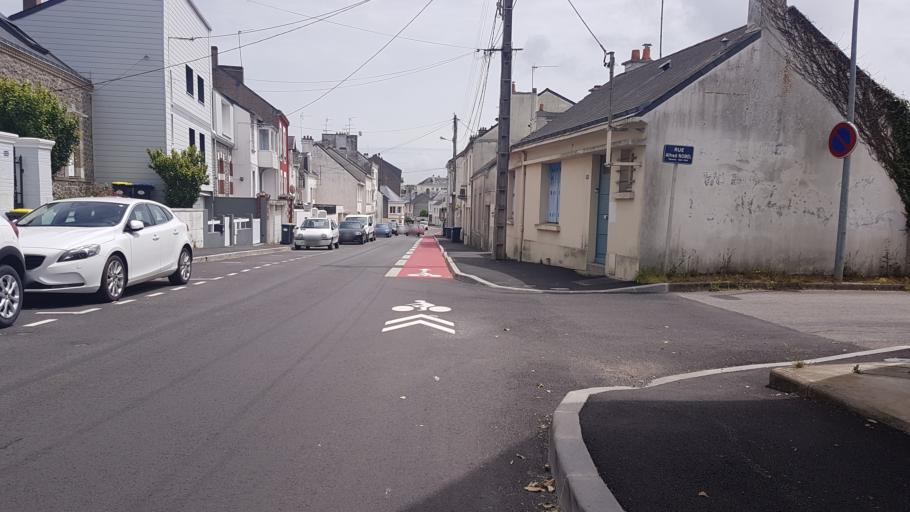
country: FR
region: Pays de la Loire
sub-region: Departement de la Loire-Atlantique
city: Saint-Nazaire
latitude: 47.2791
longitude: -2.2248
